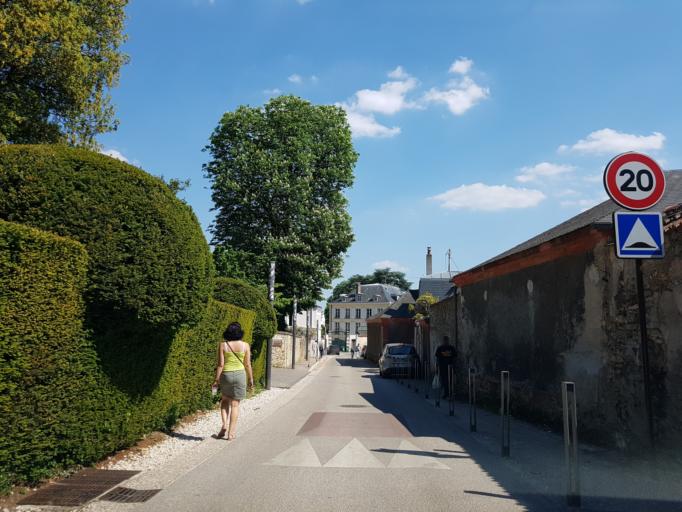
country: FR
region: Ile-de-France
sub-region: Departement des Hauts-de-Seine
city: Chatenay-Malabry
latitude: 48.7717
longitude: 2.2675
